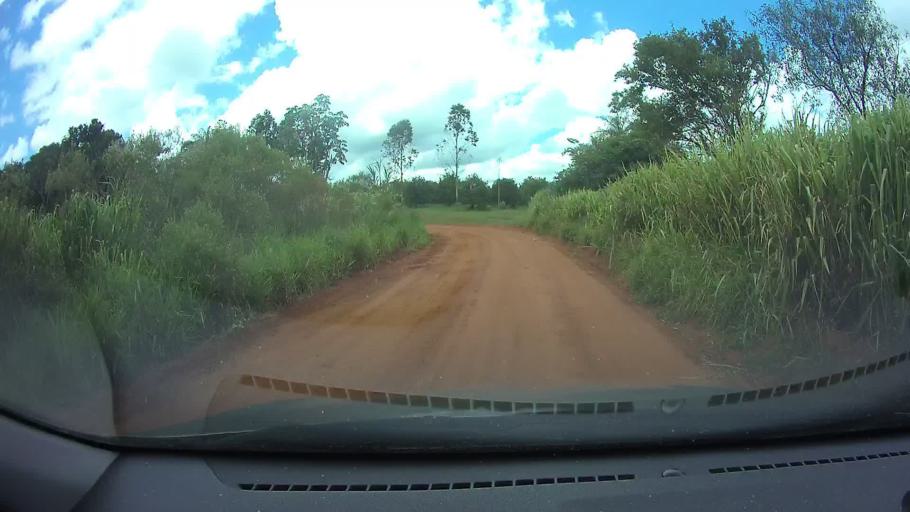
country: PY
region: Paraguari
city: La Colmena
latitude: -25.9542
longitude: -56.7699
